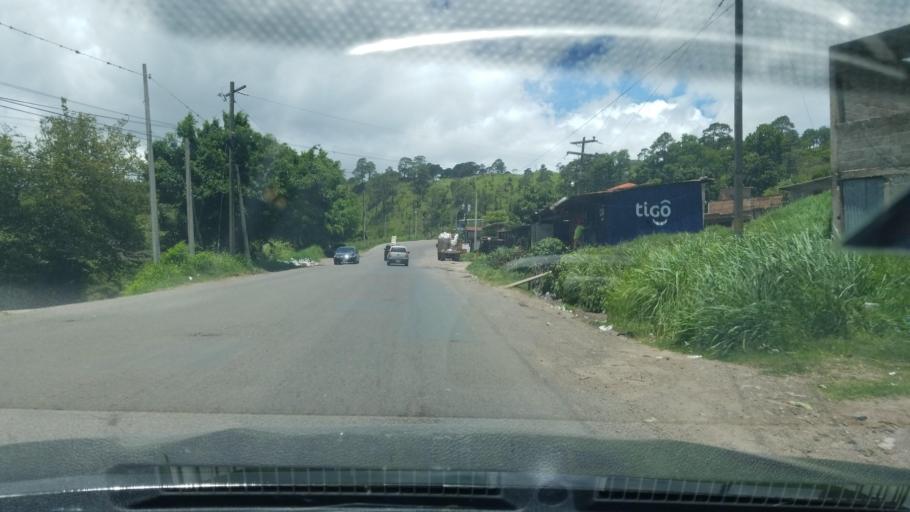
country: HN
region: Francisco Morazan
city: Rio Abajo
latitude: 14.1425
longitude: -87.2310
